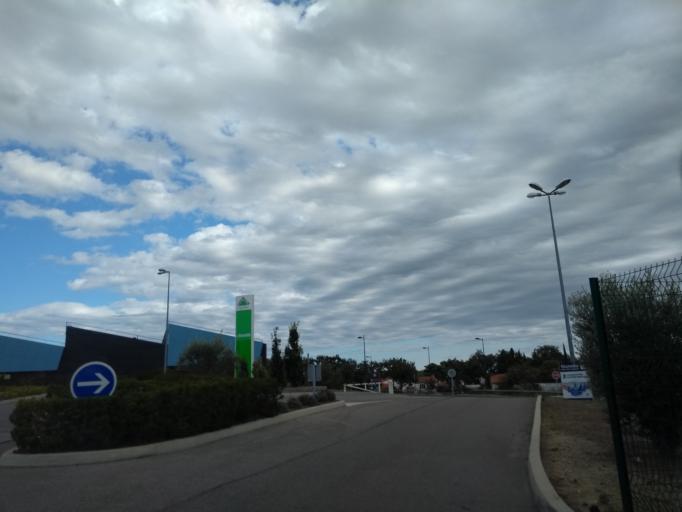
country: FR
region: Languedoc-Roussillon
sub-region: Departement des Pyrenees-Orientales
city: Pollestres
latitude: 42.6680
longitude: 2.8761
